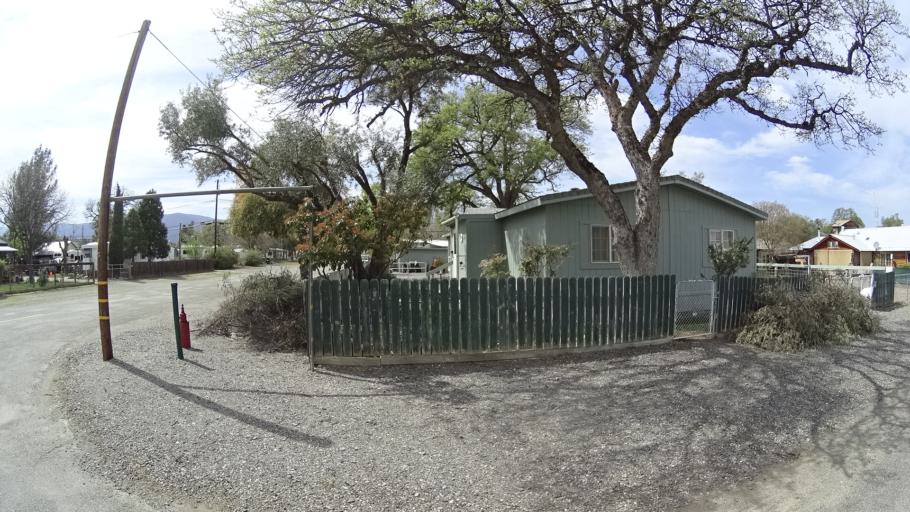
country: US
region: California
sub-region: Glenn County
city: Willows
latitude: 39.6053
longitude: -122.5384
